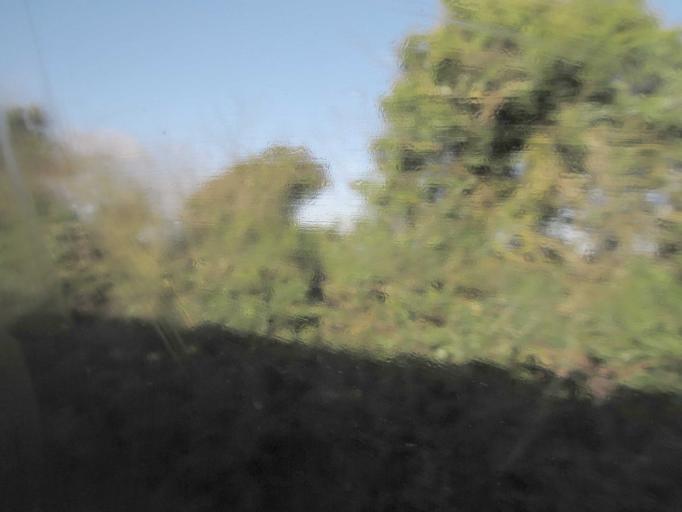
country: GB
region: England
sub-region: Hampshire
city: Overton
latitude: 51.1767
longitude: -1.2927
